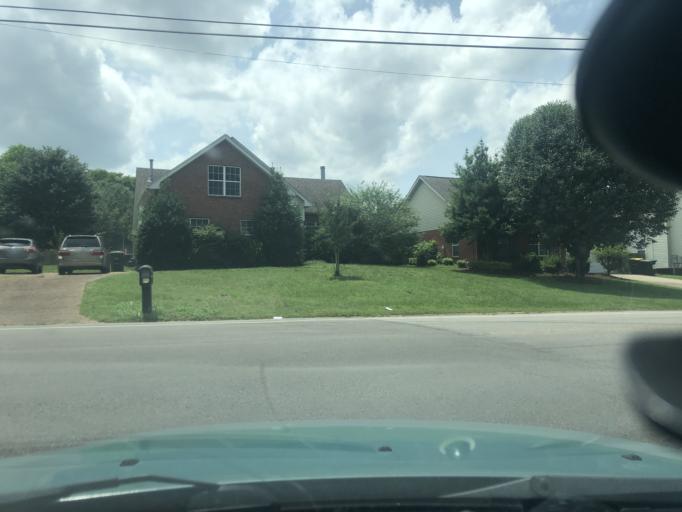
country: US
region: Tennessee
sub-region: Davidson County
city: Lakewood
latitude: 36.1334
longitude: -86.6378
